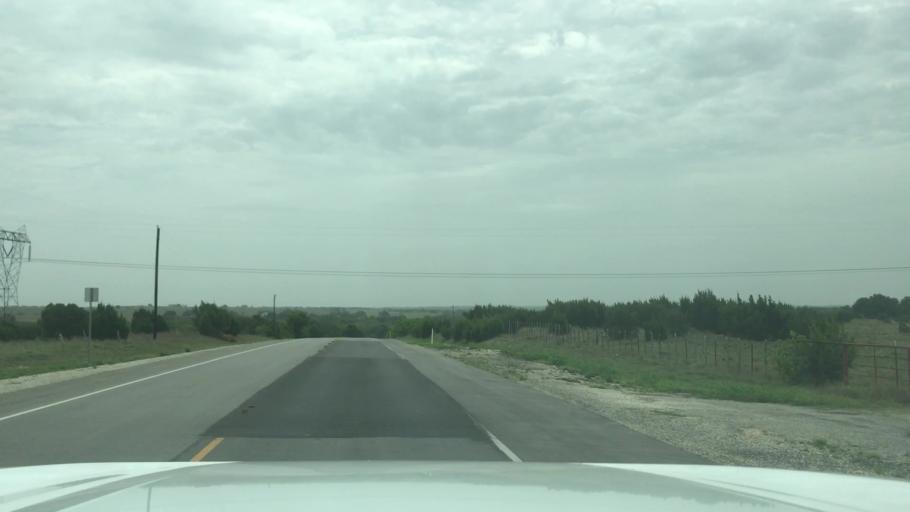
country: US
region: Texas
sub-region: Erath County
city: Dublin
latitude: 32.0769
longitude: -98.2370
